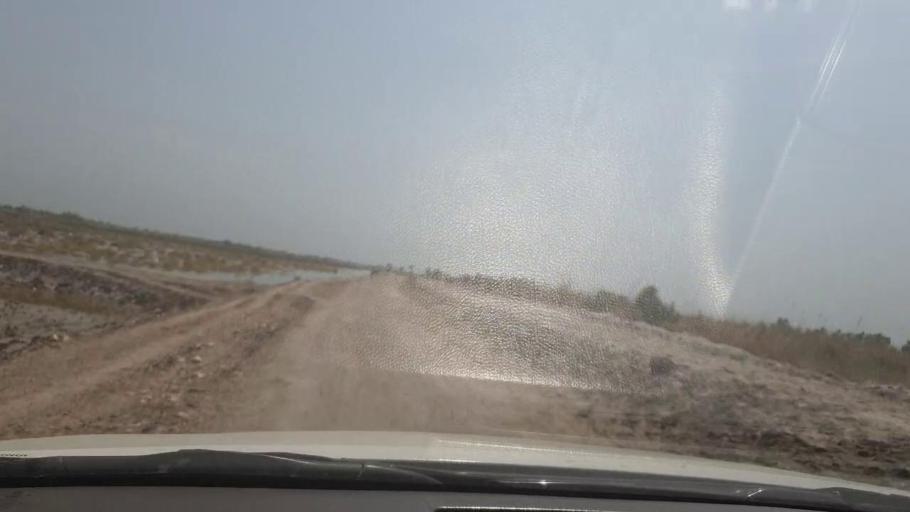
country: PK
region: Sindh
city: Shikarpur
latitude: 28.0362
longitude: 68.5737
